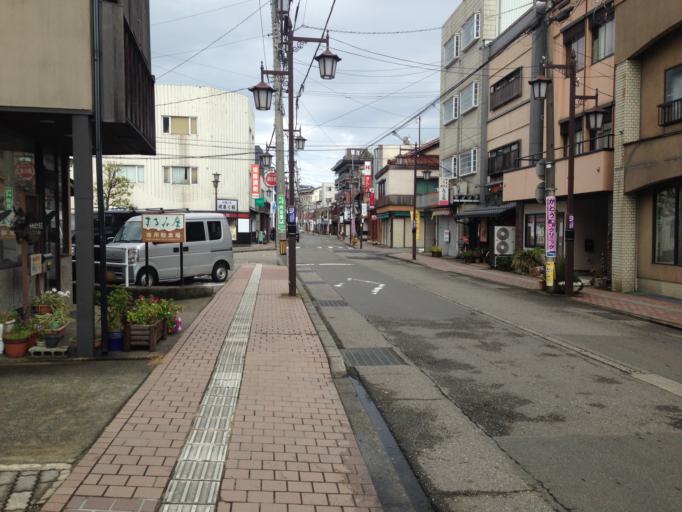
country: JP
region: Ishikawa
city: Komatsu
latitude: 36.2899
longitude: 136.3619
